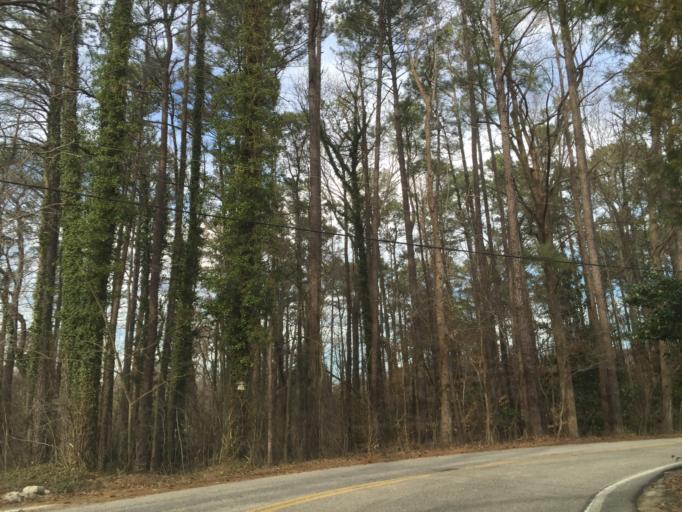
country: US
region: Virginia
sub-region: City of Newport News
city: Newport News
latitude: 37.0840
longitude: -76.5151
